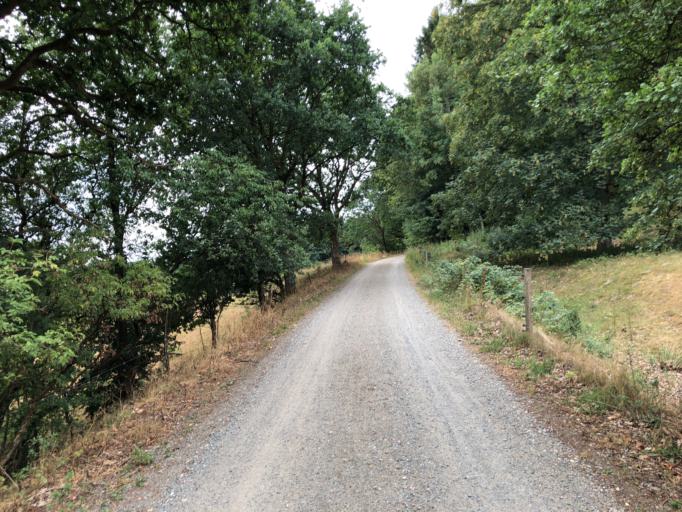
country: DK
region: South Denmark
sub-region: Vejle Kommune
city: Egtved
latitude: 55.6577
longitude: 9.2858
